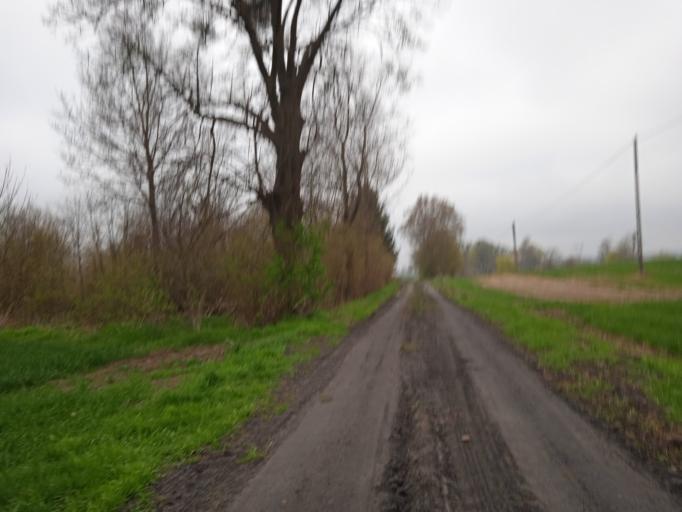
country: PL
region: Kujawsko-Pomorskie
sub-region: Powiat grudziadzki
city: Lasin
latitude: 53.5726
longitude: 19.0545
